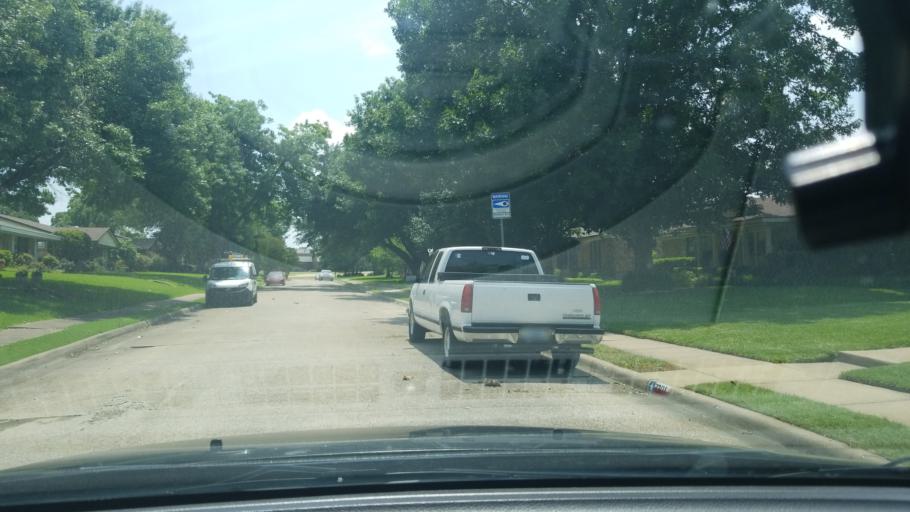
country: US
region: Texas
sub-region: Dallas County
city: Mesquite
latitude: 32.8013
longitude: -96.6347
